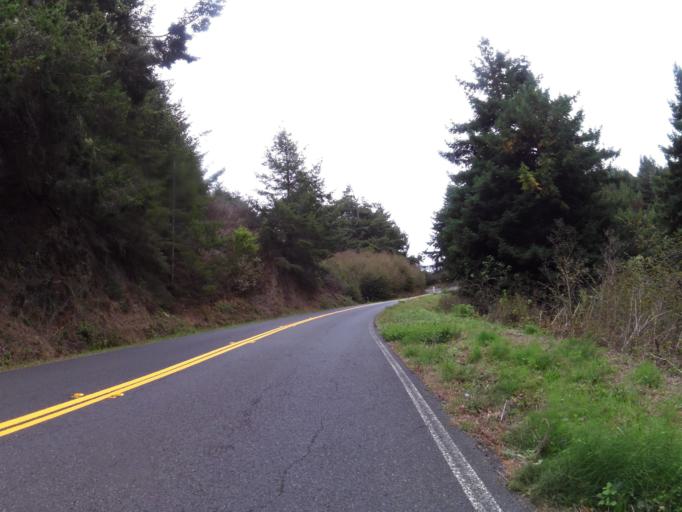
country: US
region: California
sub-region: Sonoma County
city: Monte Rio
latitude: 38.5165
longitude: -123.2410
